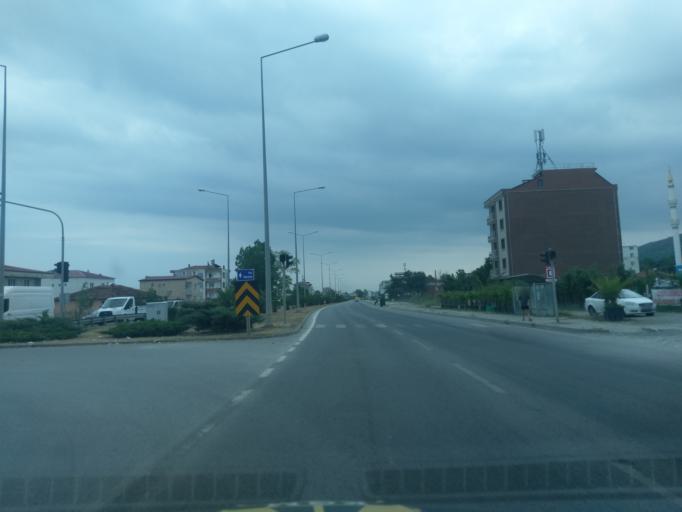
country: TR
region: Samsun
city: Taflan
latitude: 41.4037
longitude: 36.1857
